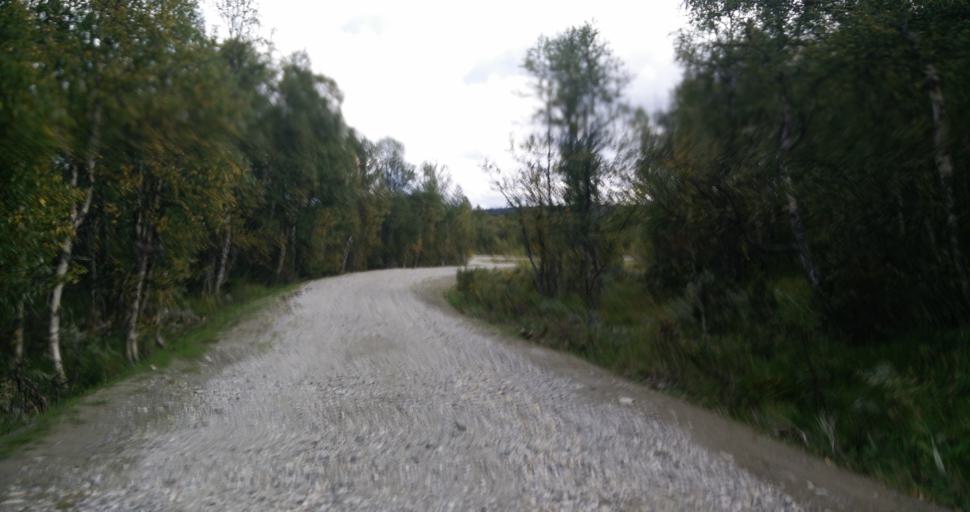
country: NO
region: Sor-Trondelag
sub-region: Tydal
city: Aas
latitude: 62.6356
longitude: 12.4186
